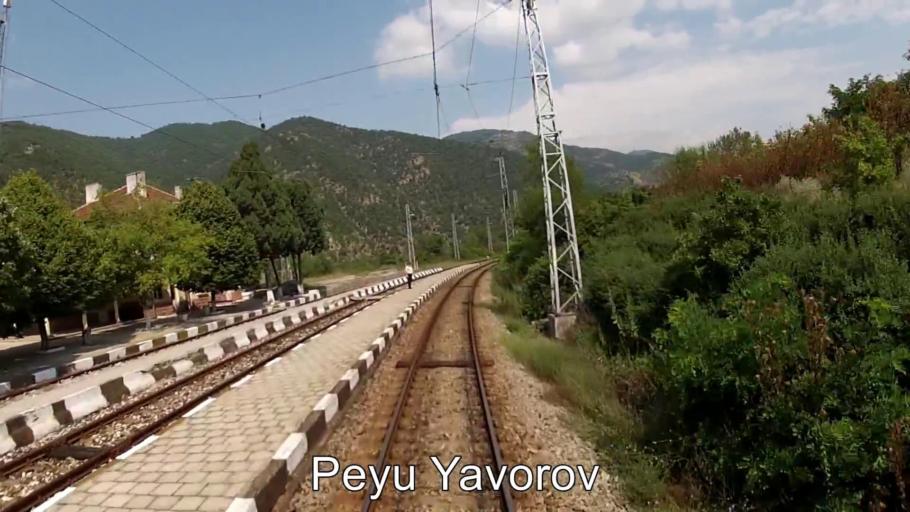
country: BG
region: Blagoevgrad
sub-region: Obshtina Kresna
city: Kresna
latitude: 41.7303
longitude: 23.1570
